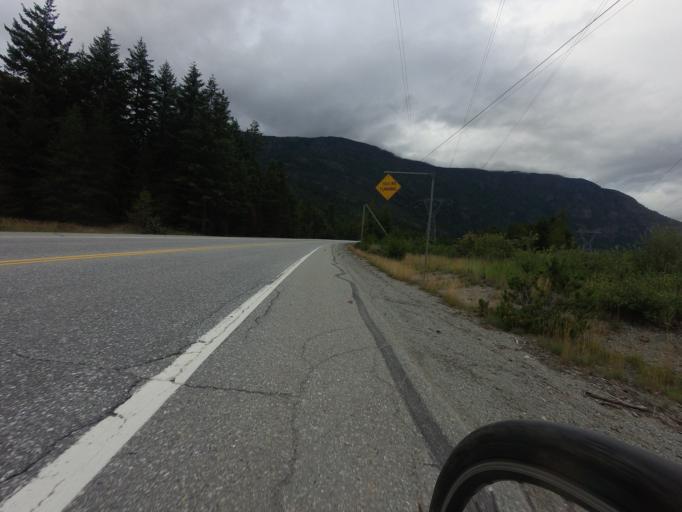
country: CA
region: British Columbia
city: Pemberton
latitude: 50.2651
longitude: -122.8668
